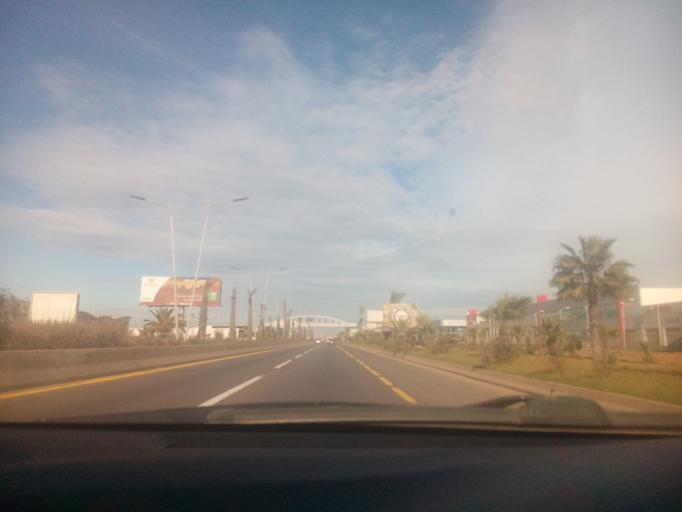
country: DZ
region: Oran
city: Es Senia
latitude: 35.6373
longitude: -0.5882
